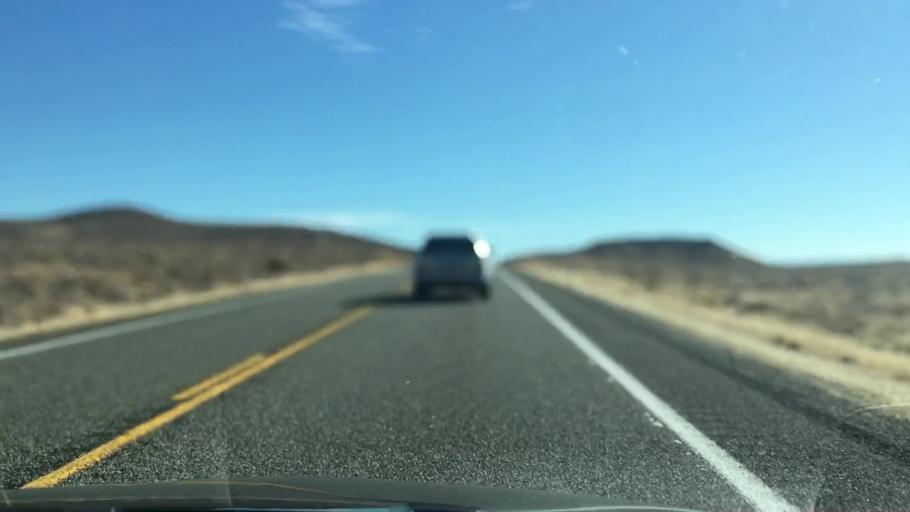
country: US
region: Nevada
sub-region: Lyon County
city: Silver Springs
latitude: 39.2319
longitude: -119.2308
